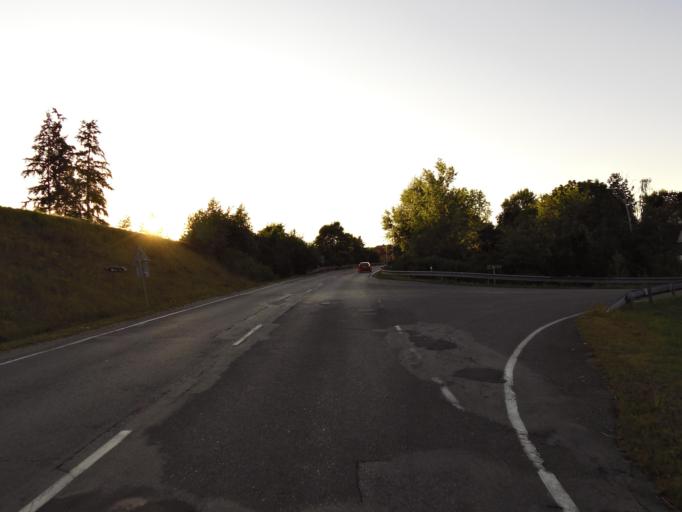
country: CZ
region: Central Bohemia
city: Mnichovo Hradiste
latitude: 50.5201
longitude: 14.9448
